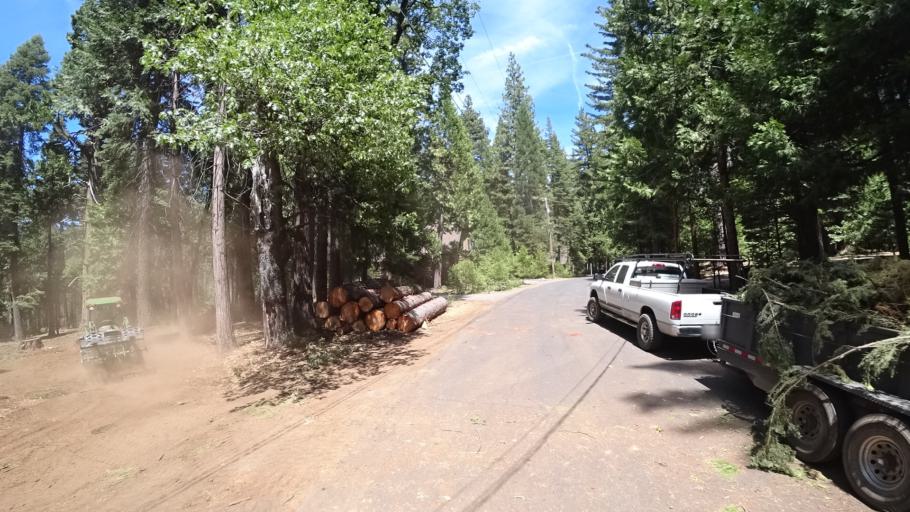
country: US
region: California
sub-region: Calaveras County
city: Arnold
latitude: 38.3112
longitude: -120.2672
